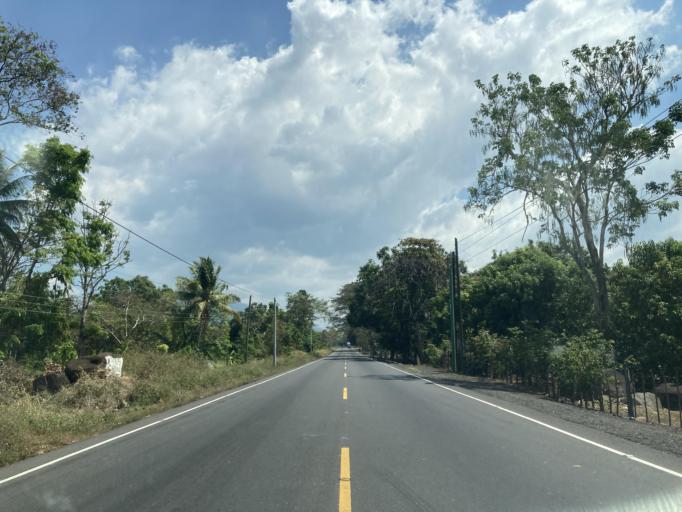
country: GT
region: Santa Rosa
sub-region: Municipio de Taxisco
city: Taxisco
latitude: 14.0933
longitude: -90.5546
